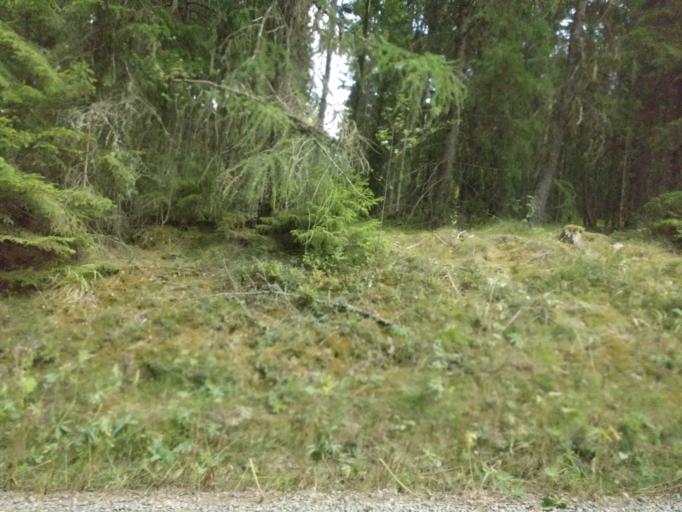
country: SE
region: Vaermland
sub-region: Hagfors Kommun
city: Hagfors
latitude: 60.0176
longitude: 13.7023
